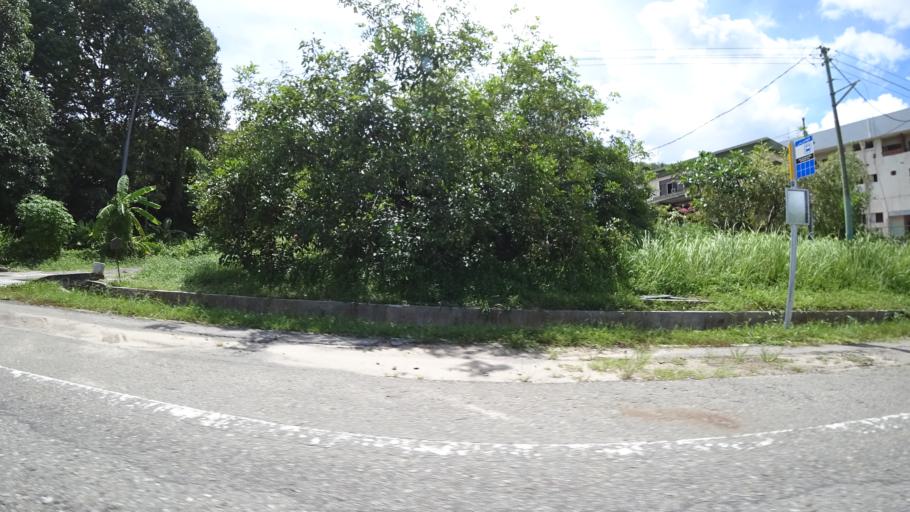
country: BN
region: Brunei and Muara
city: Bandar Seri Begawan
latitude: 4.8881
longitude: 114.9740
